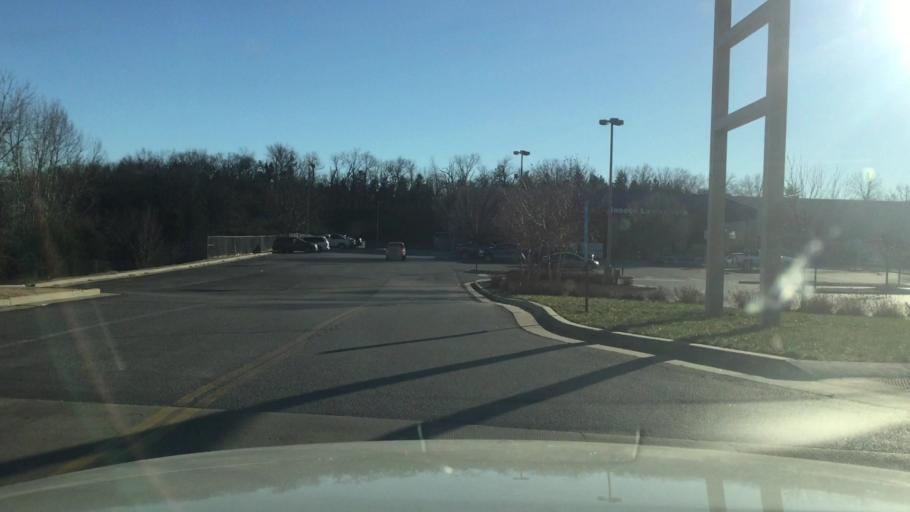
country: US
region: Missouri
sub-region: Cole County
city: Jefferson City
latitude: 38.5814
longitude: -92.2429
